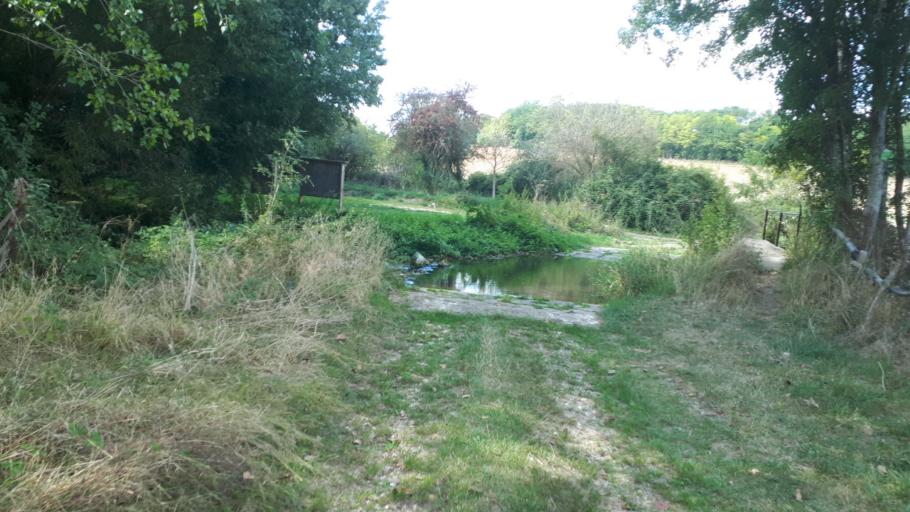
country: FR
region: Centre
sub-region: Departement du Loir-et-Cher
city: Villiers-sur-Loir
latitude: 47.8224
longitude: 0.9677
